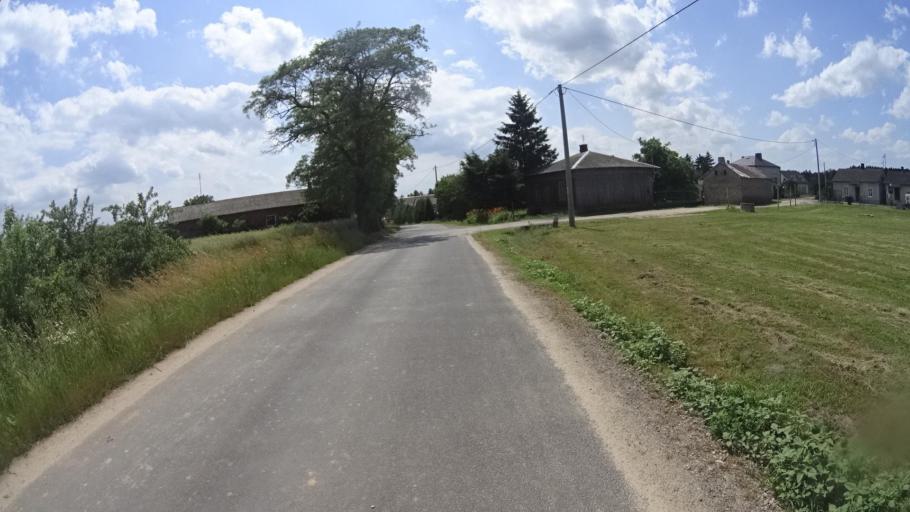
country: PL
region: Masovian Voivodeship
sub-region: Powiat grojecki
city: Goszczyn
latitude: 51.7139
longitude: 20.8325
